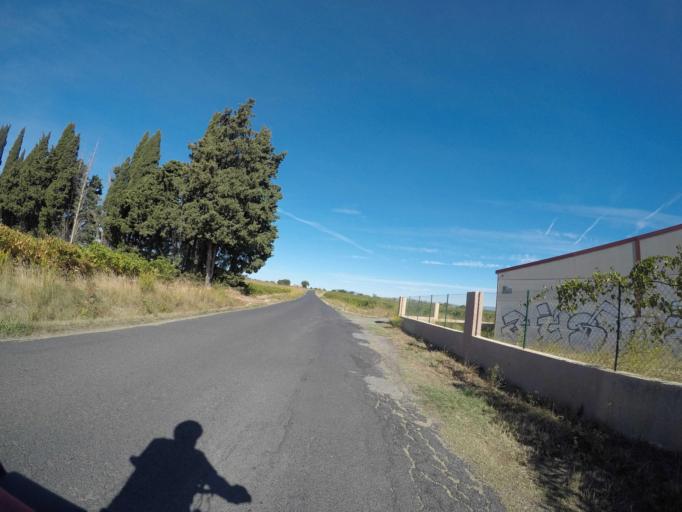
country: FR
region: Languedoc-Roussillon
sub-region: Departement des Pyrenees-Orientales
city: Ponteilla
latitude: 42.6328
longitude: 2.8095
